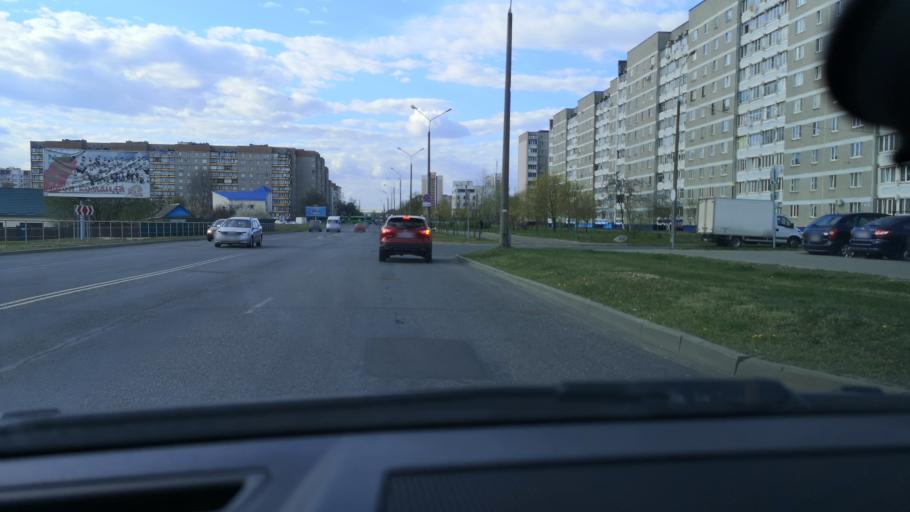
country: BY
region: Gomel
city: Gomel
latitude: 52.4003
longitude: 30.9223
